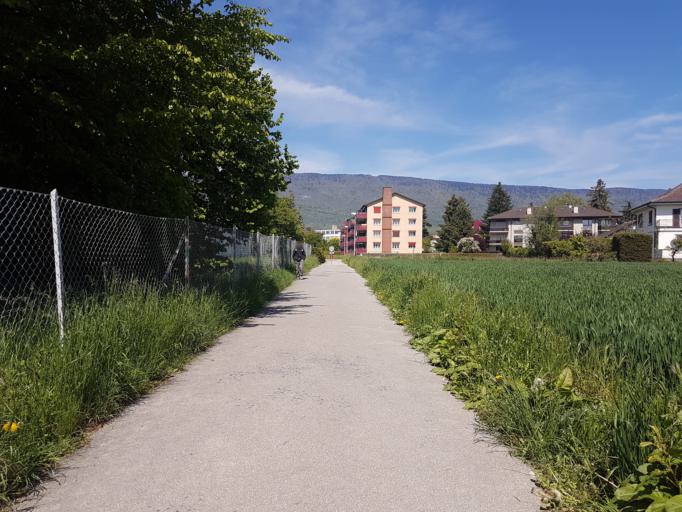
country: CH
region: Neuchatel
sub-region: Neuchatel District
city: Saint-Blaise
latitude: 47.0073
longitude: 7.0106
